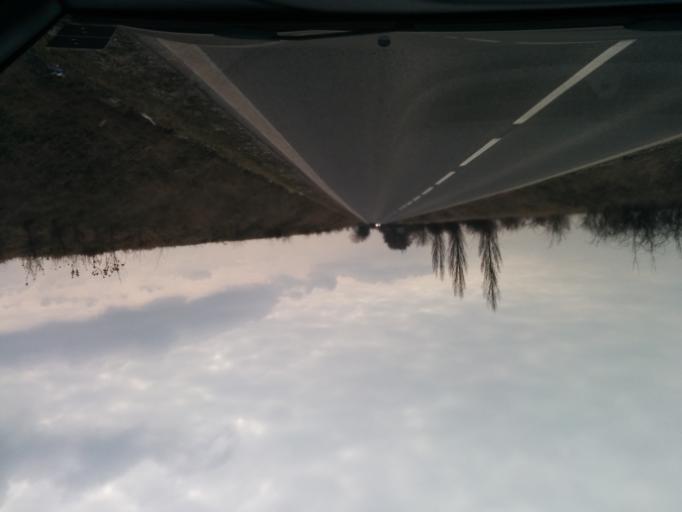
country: SK
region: Trnavsky
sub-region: Okres Trnava
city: Trnava
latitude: 48.3132
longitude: 17.6035
